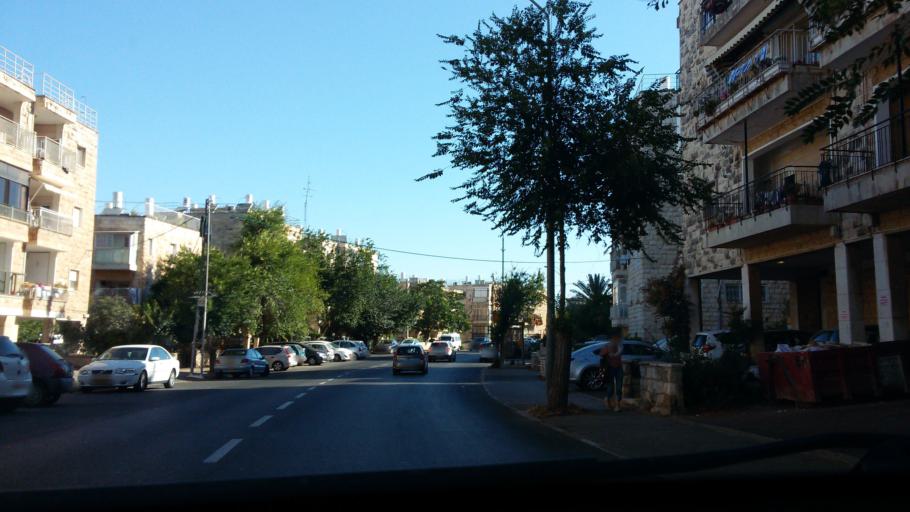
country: IL
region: Jerusalem
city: Jerusalem
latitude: 31.7667
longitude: 35.2060
